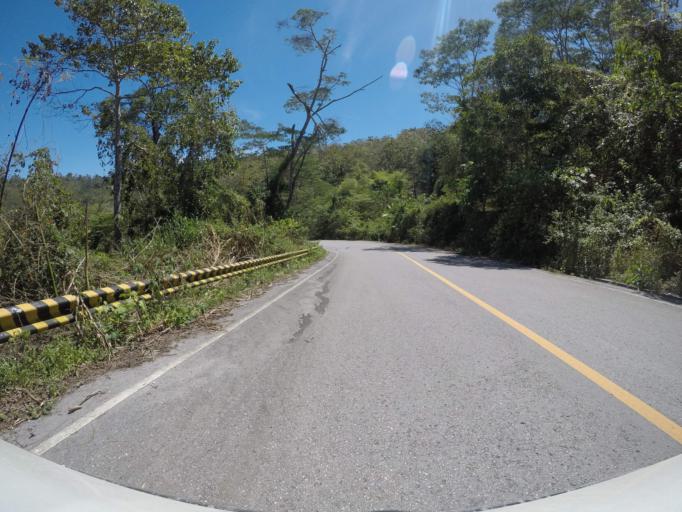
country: TL
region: Manatuto
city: Manatuto
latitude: -8.8210
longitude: 125.9791
